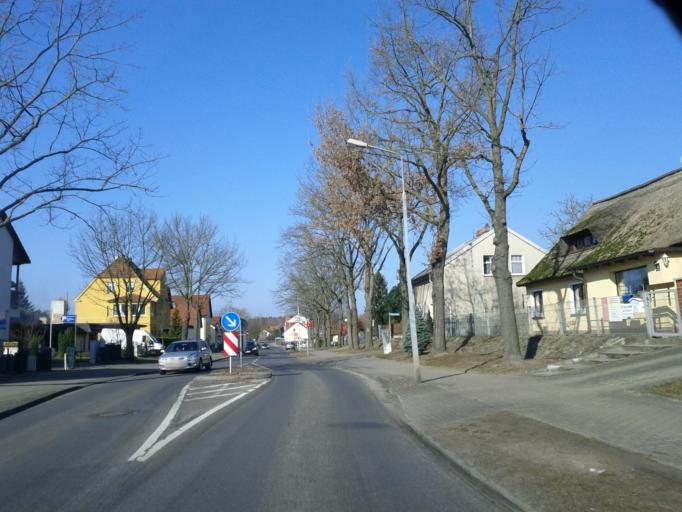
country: DE
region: Brandenburg
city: Grunheide
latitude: 52.4179
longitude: 13.8013
